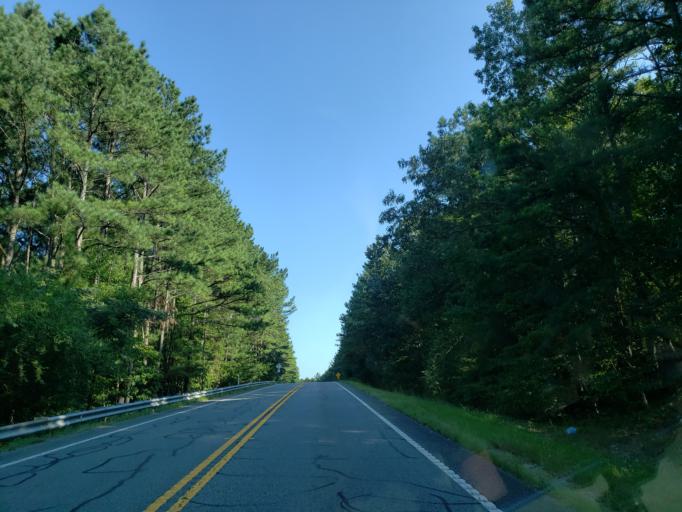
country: US
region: Georgia
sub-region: Whitfield County
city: Varnell
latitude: 34.9021
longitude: -84.9914
